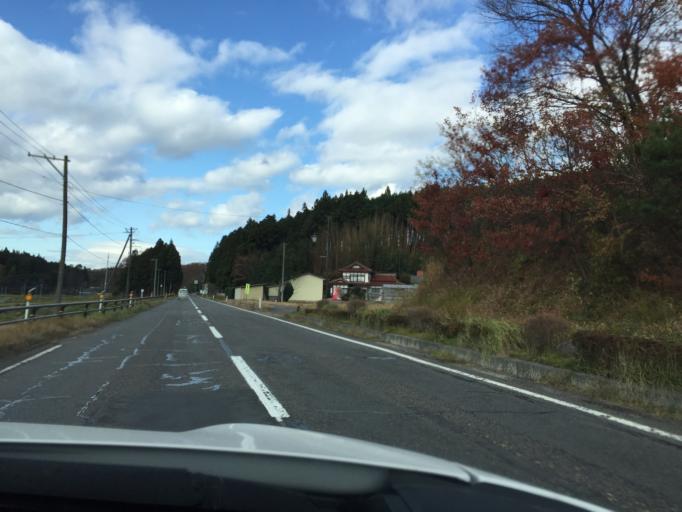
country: JP
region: Fukushima
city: Ishikawa
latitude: 37.2619
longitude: 140.5565
